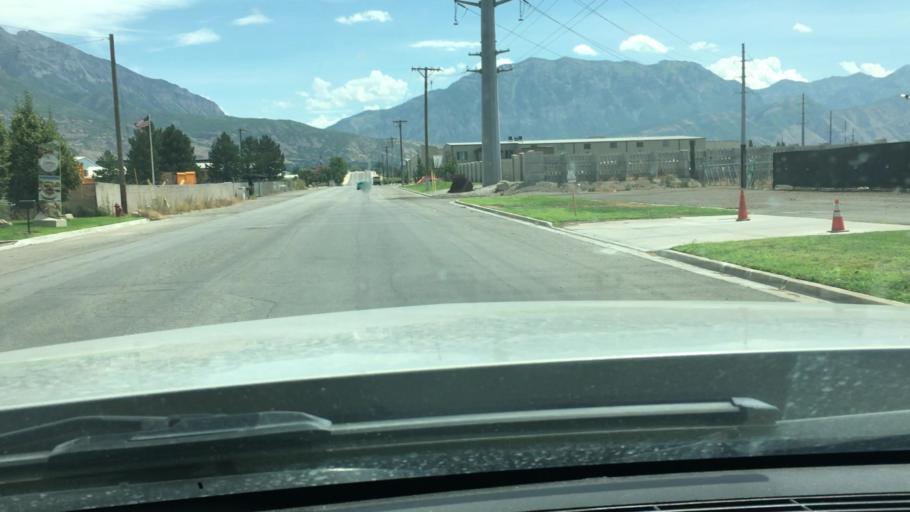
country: US
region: Utah
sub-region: Utah County
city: Lindon
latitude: 40.3335
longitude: -111.7523
